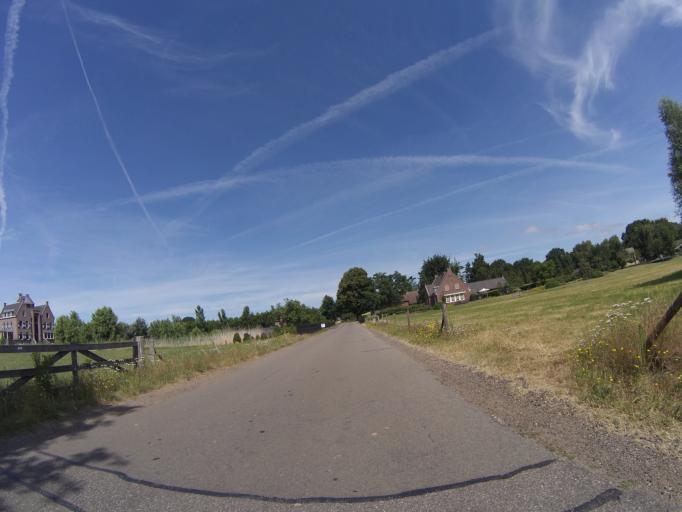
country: NL
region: Gelderland
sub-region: Gemeente Ermelo
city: Horst
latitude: 52.3182
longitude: 5.5836
